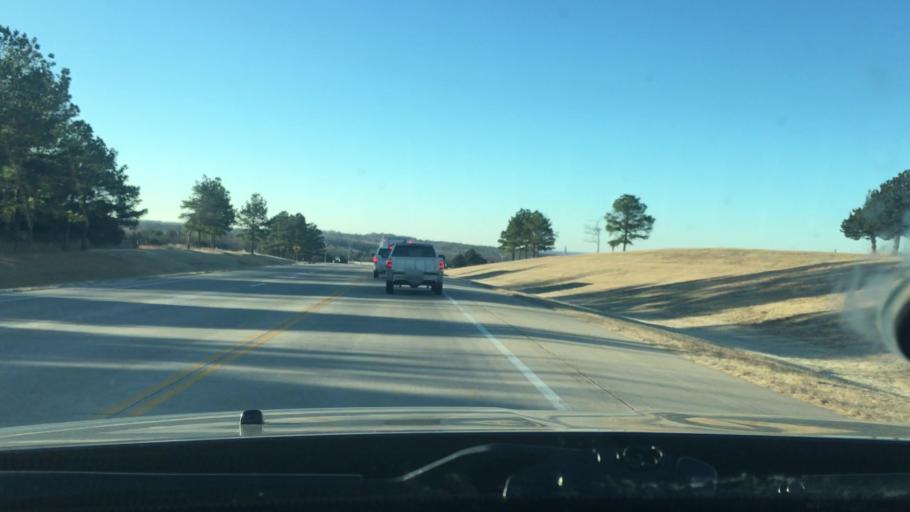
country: US
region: Oklahoma
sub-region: Murray County
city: Sulphur
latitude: 34.5109
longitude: -97.0107
